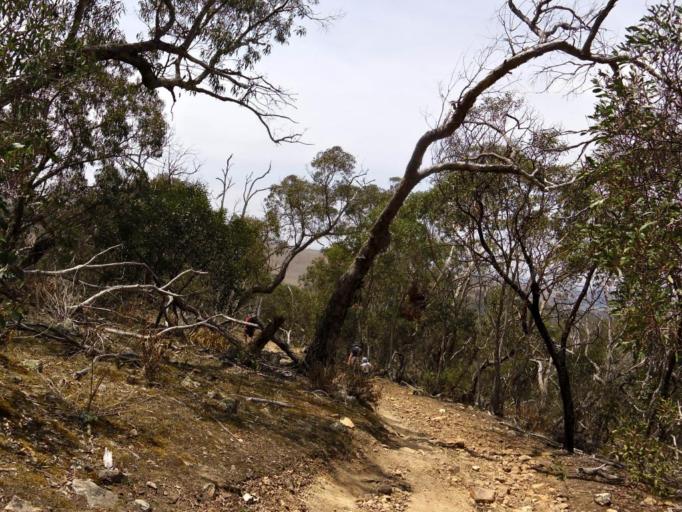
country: AU
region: Victoria
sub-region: Moorabool
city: Bacchus Marsh
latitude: -37.6607
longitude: 144.3588
